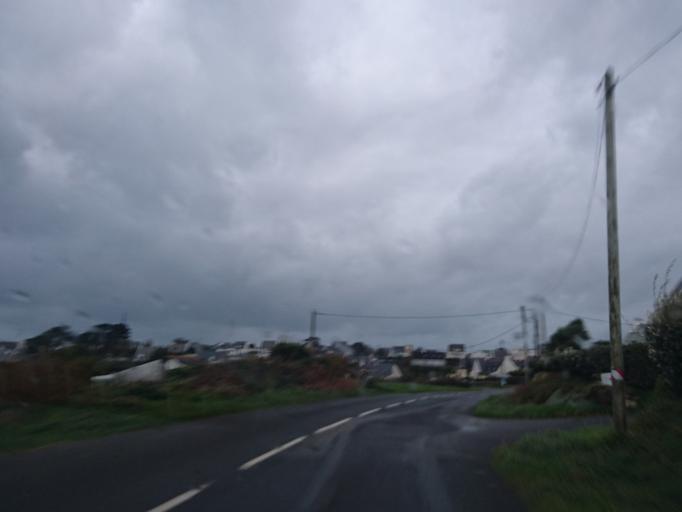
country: FR
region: Brittany
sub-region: Departement du Finistere
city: Le Conquet
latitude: 48.3510
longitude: -4.7731
